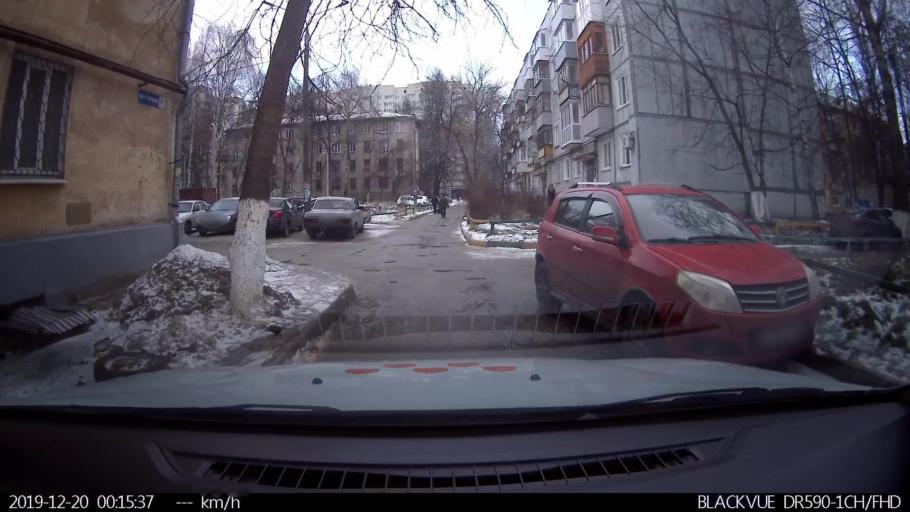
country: RU
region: Jaroslavl
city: Porech'ye-Rybnoye
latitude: 56.9829
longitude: 39.3910
